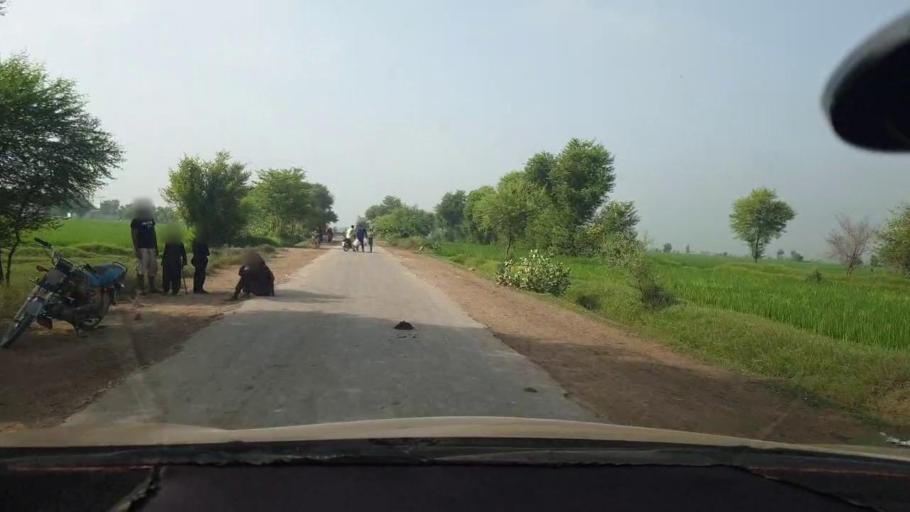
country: PK
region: Sindh
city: Goth Garelo
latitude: 27.4923
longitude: 68.0104
